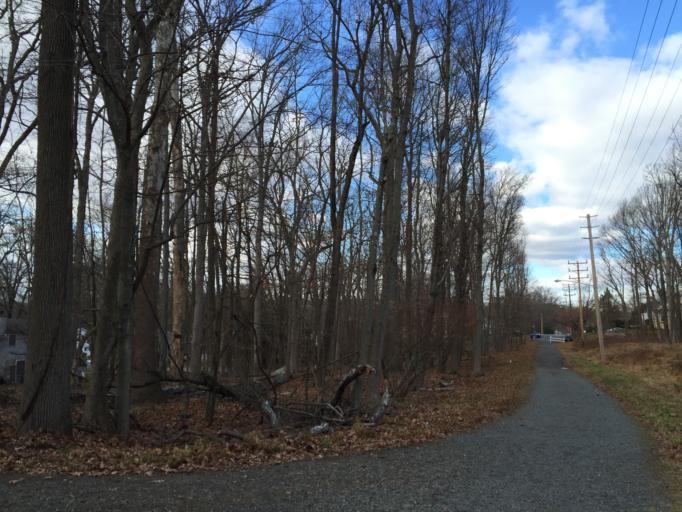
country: US
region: New Jersey
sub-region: Union County
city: New Providence
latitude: 40.6945
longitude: -74.3967
